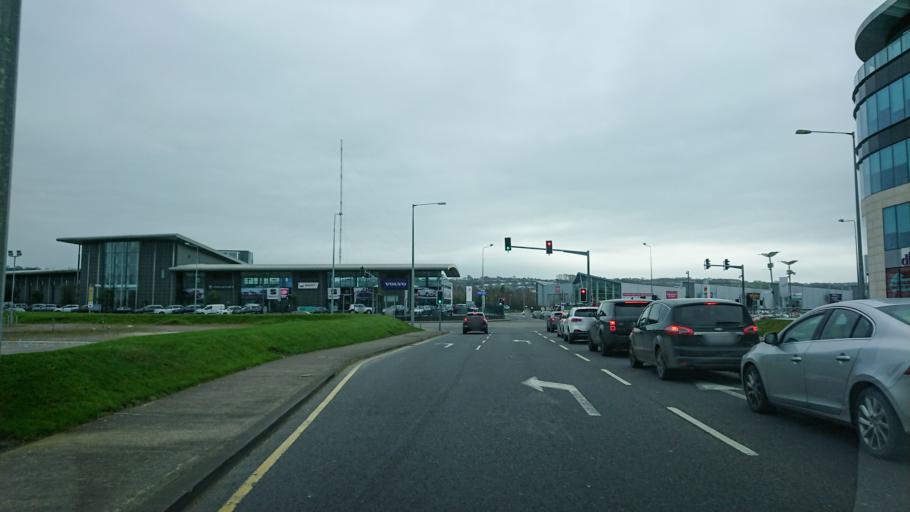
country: IE
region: Munster
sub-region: County Cork
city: Passage West
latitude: 51.8863
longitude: -8.4014
